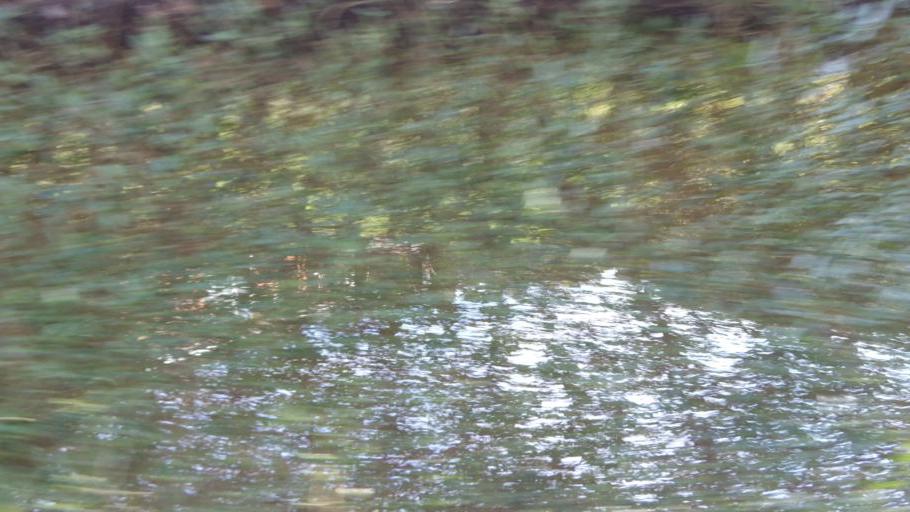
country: DK
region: Central Jutland
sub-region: Arhus Kommune
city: Kolt
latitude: 56.1062
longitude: 10.0860
